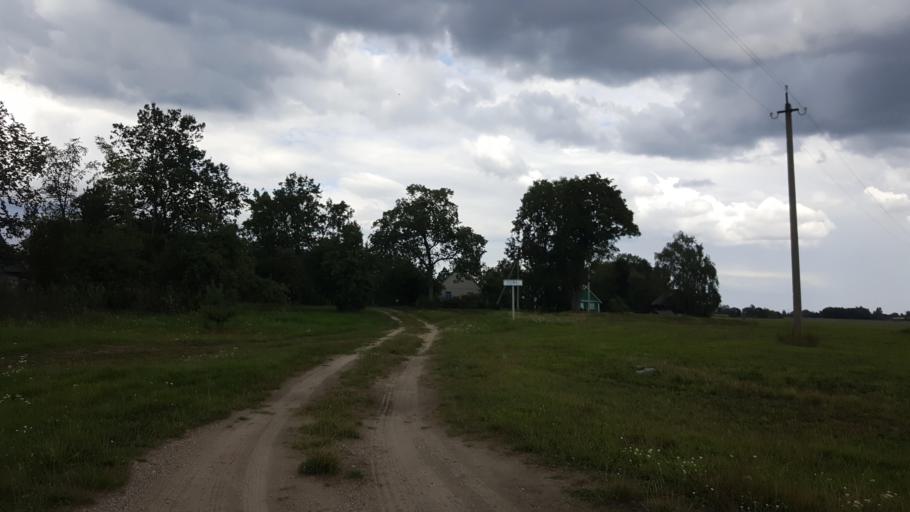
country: BY
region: Brest
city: Zhabinka
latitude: 52.2597
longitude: 23.9711
